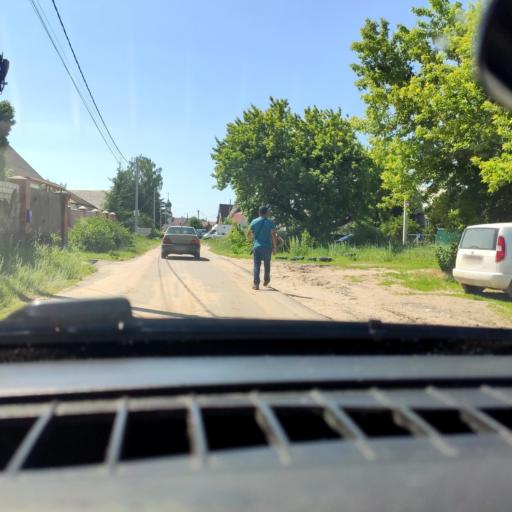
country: RU
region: Voronezj
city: Podgornoye
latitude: 51.7901
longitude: 39.1425
